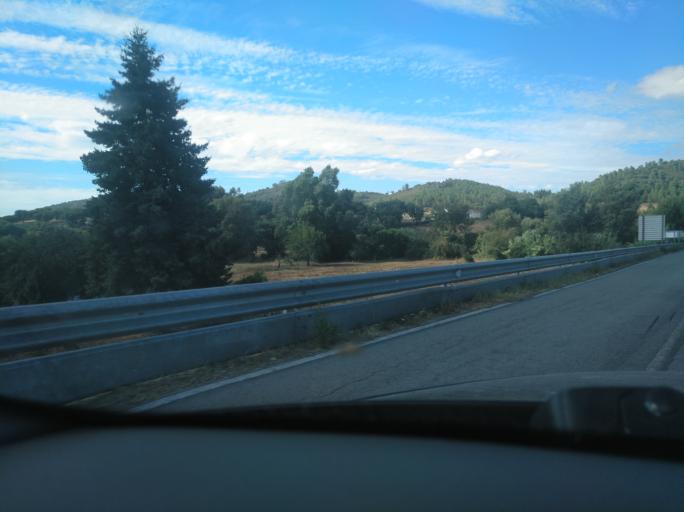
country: ES
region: Extremadura
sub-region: Provincia de Badajoz
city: La Codosera
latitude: 39.1797
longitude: -7.1768
